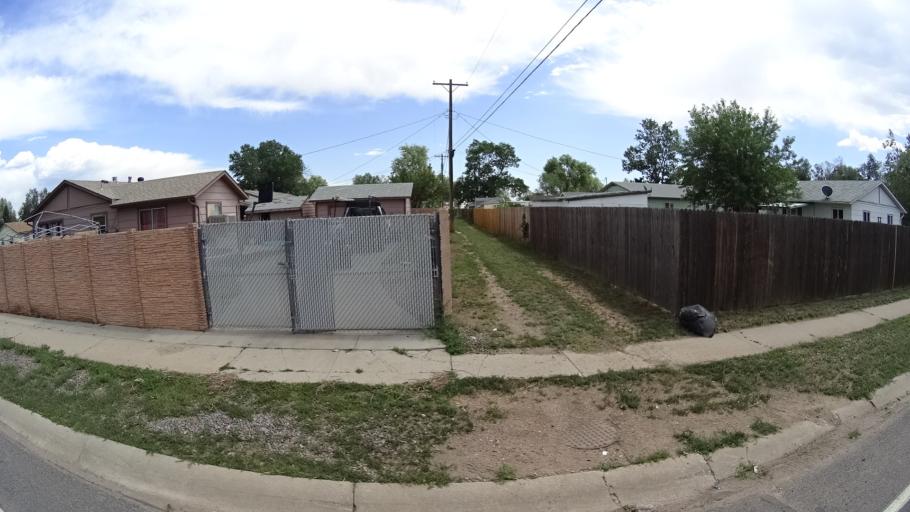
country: US
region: Colorado
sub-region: El Paso County
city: Stratmoor
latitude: 38.7979
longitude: -104.8035
